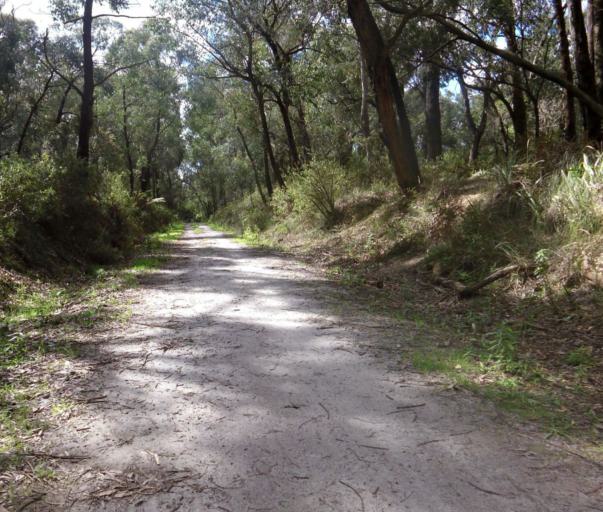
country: AU
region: Victoria
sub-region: Bass Coast
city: North Wonthaggi
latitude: -38.6163
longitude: 146.0422
